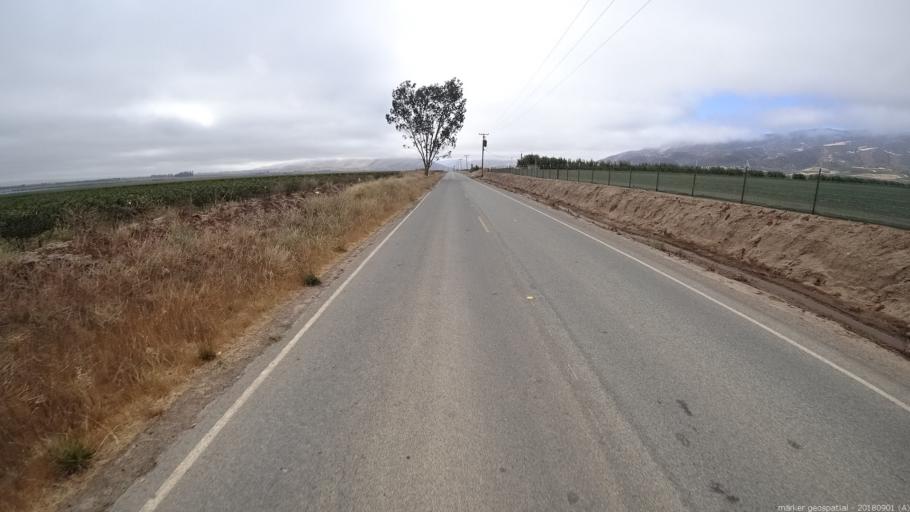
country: US
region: California
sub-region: Monterey County
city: Greenfield
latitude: 36.3417
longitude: -121.3186
